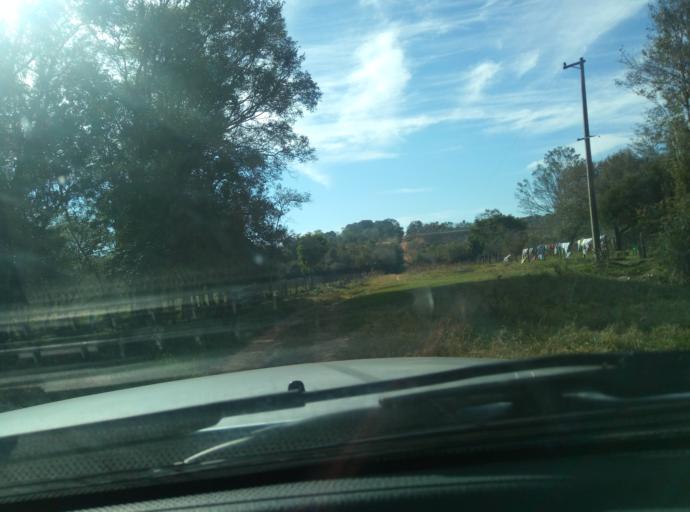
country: PY
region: Caaguazu
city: Carayao
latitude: -25.1664
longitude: -56.2928
